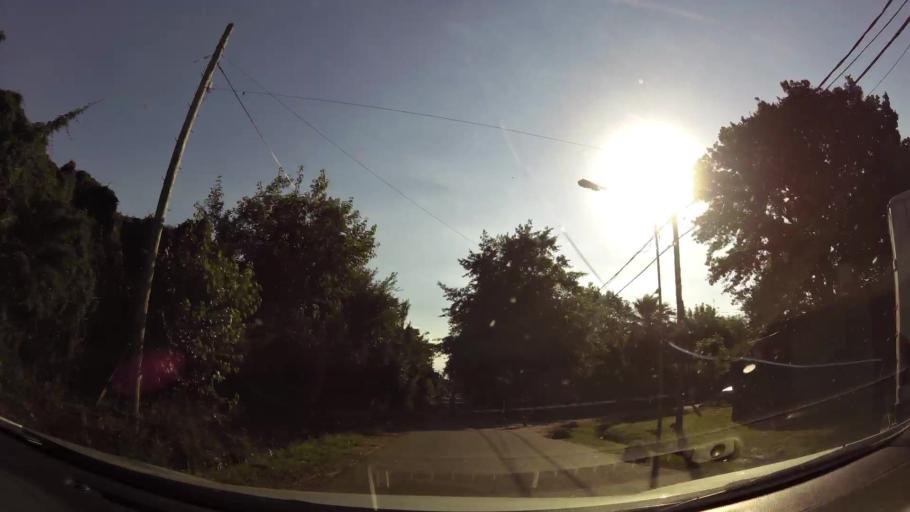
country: AR
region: Buenos Aires
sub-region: Partido de Tigre
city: Tigre
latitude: -34.4740
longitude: -58.6381
